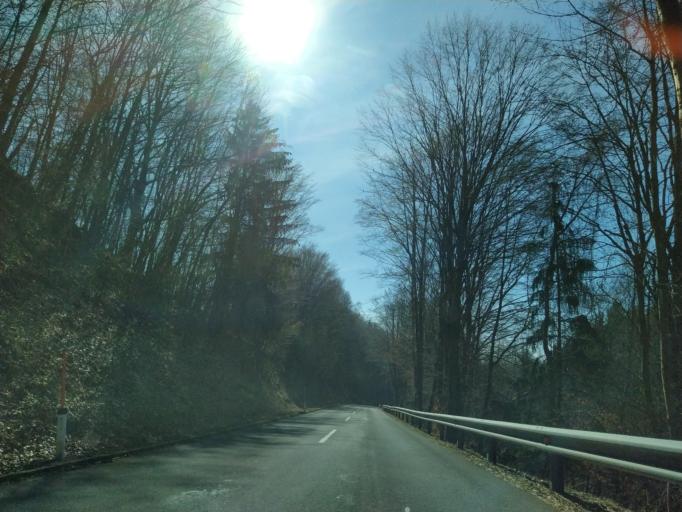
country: AT
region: Upper Austria
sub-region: Politischer Bezirk Urfahr-Umgebung
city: Kirchschlag bei Linz
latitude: 48.3911
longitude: 14.2877
